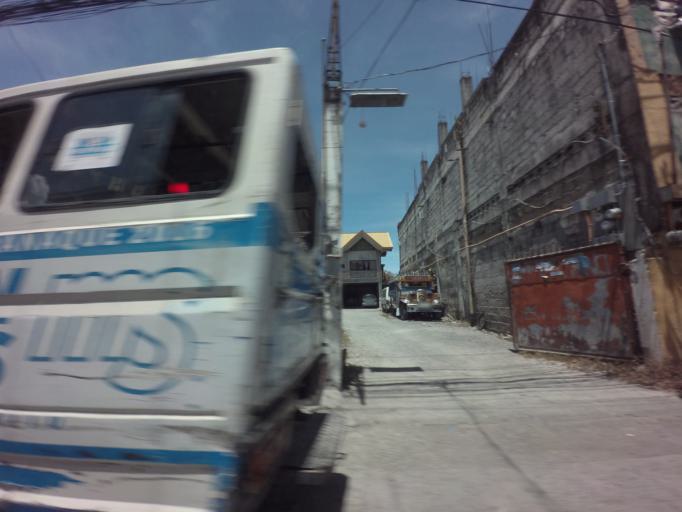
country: PH
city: Sambayanihan People's Village
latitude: 14.4923
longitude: 120.9897
